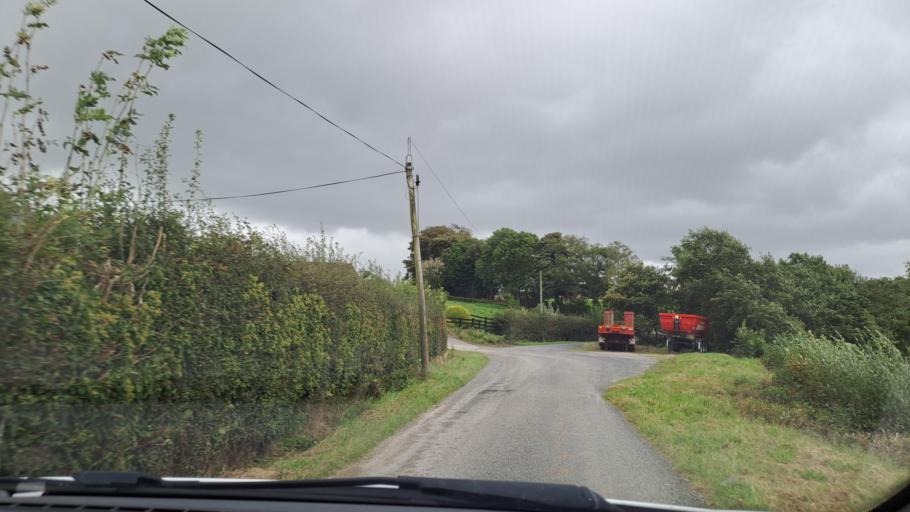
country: IE
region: Ulster
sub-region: An Cabhan
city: Kingscourt
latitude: 53.9738
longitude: -6.8647
